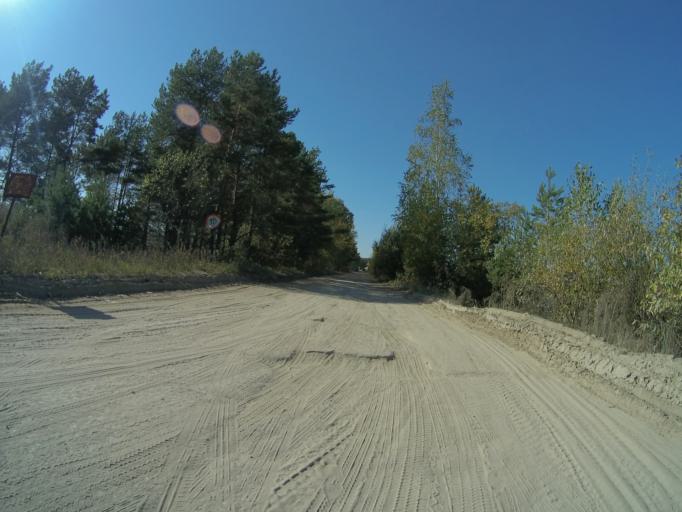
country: RU
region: Vladimir
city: Raduzhnyy
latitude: 56.0294
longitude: 40.3334
